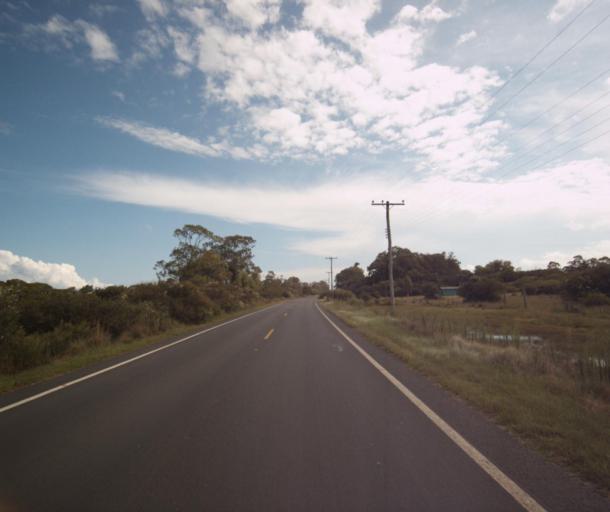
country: BR
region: Rio Grande do Sul
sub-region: Sao Lourenco Do Sul
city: Sao Lourenco do Sul
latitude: -31.6188
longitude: -51.4031
